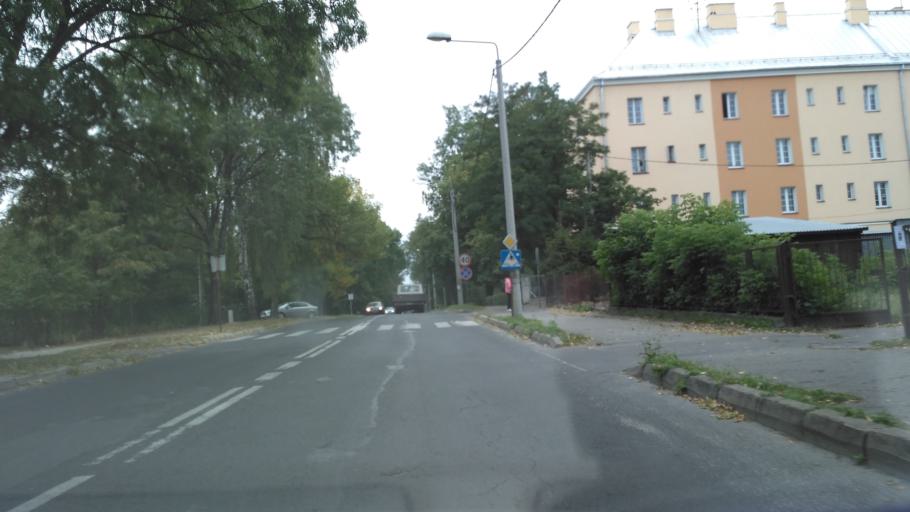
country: PL
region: Lublin Voivodeship
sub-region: Chelm
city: Chelm
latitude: 51.1430
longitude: 23.4465
